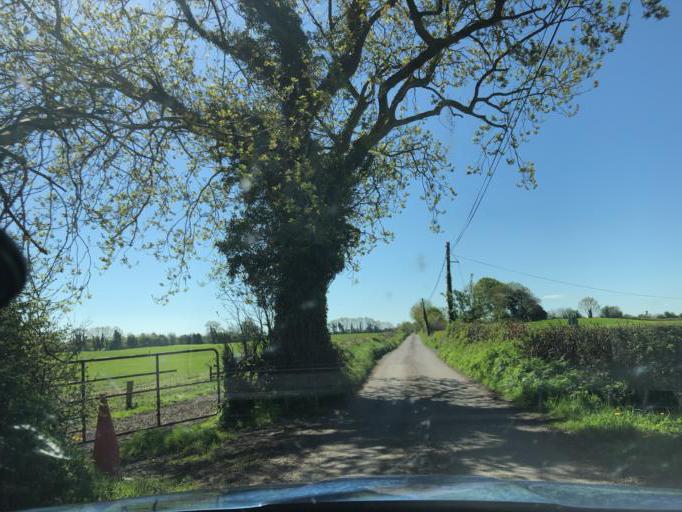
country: IE
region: Connaught
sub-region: County Galway
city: Portumna
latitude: 53.1473
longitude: -8.3393
